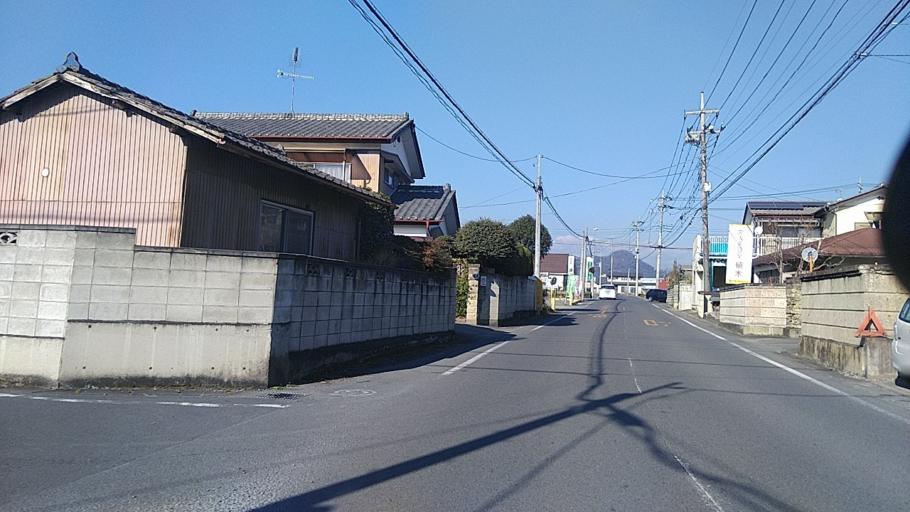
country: JP
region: Tochigi
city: Tanuma
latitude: 36.3610
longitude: 139.5600
